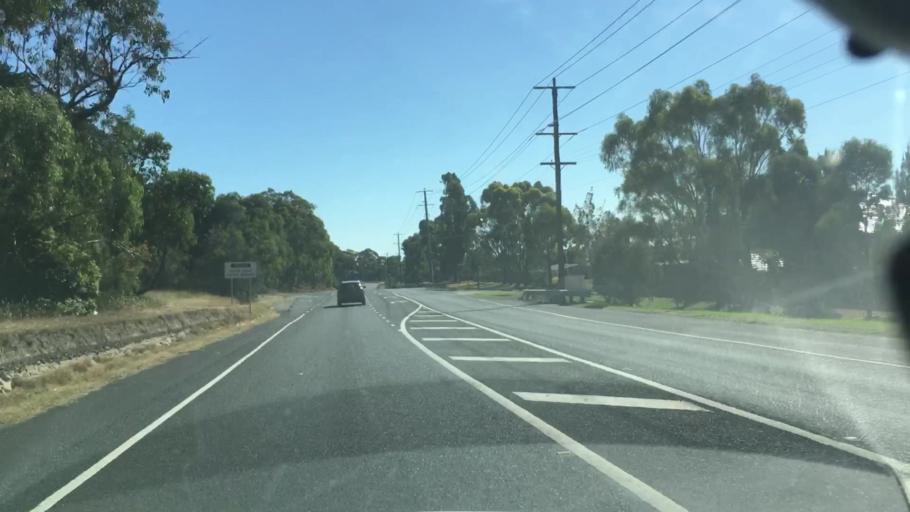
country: AU
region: Victoria
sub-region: Yarra Ranges
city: Lysterfield
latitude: -37.9278
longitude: 145.2748
